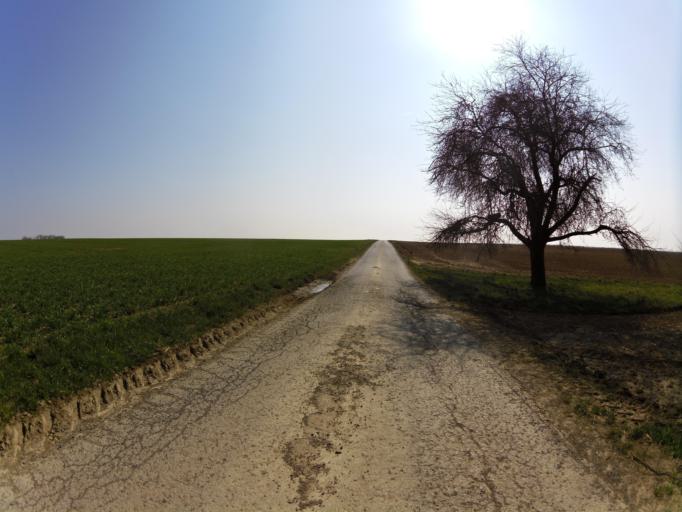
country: DE
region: Bavaria
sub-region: Regierungsbezirk Unterfranken
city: Eibelstadt
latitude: 49.6952
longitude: 9.9814
